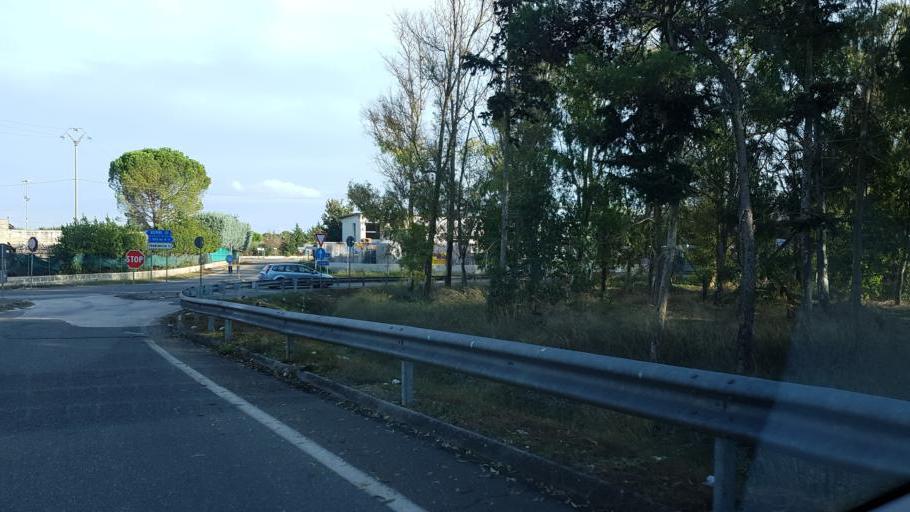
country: IT
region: Apulia
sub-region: Provincia di Brindisi
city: Francavilla Fontana
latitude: 40.5471
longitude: 17.5926
